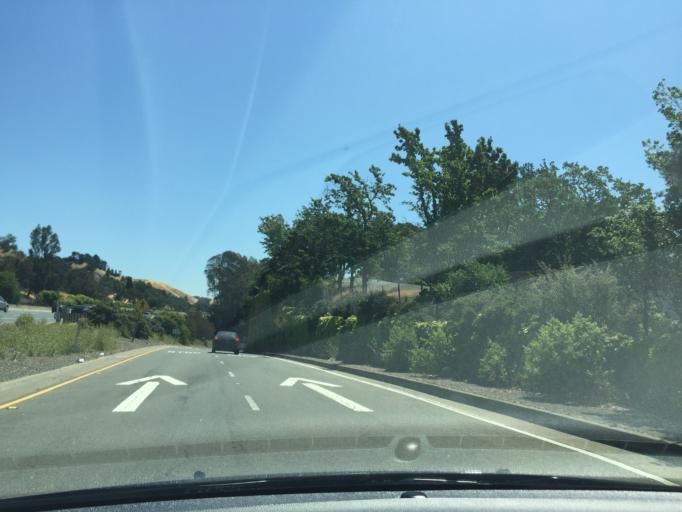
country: US
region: California
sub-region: Contra Costa County
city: Lafayette
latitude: 37.8932
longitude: -122.1231
